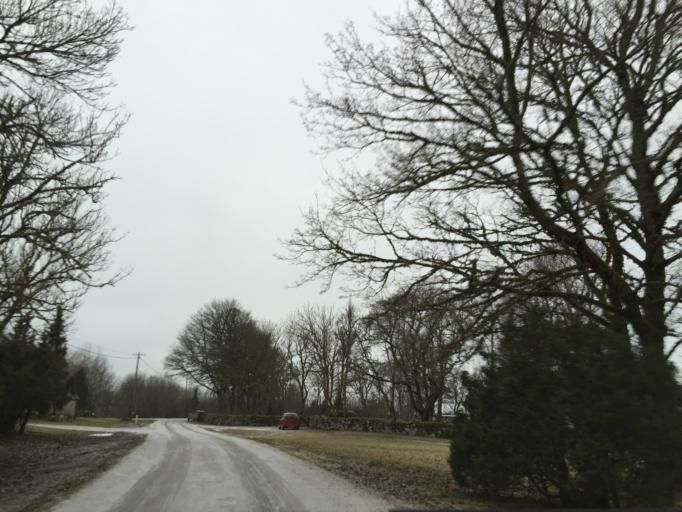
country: EE
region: Saare
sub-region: Orissaare vald
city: Orissaare
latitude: 58.5957
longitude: 23.0815
